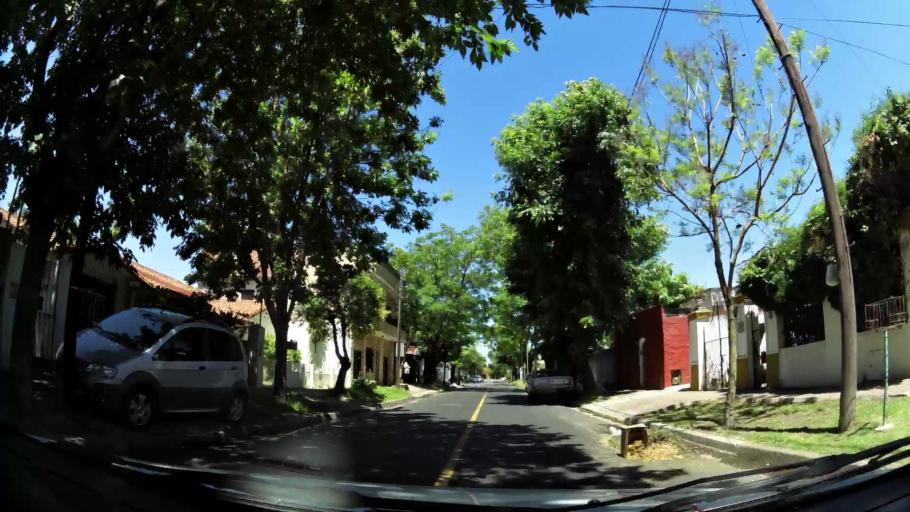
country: AR
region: Buenos Aires
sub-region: Partido de San Isidro
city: San Isidro
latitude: -34.5109
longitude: -58.5572
